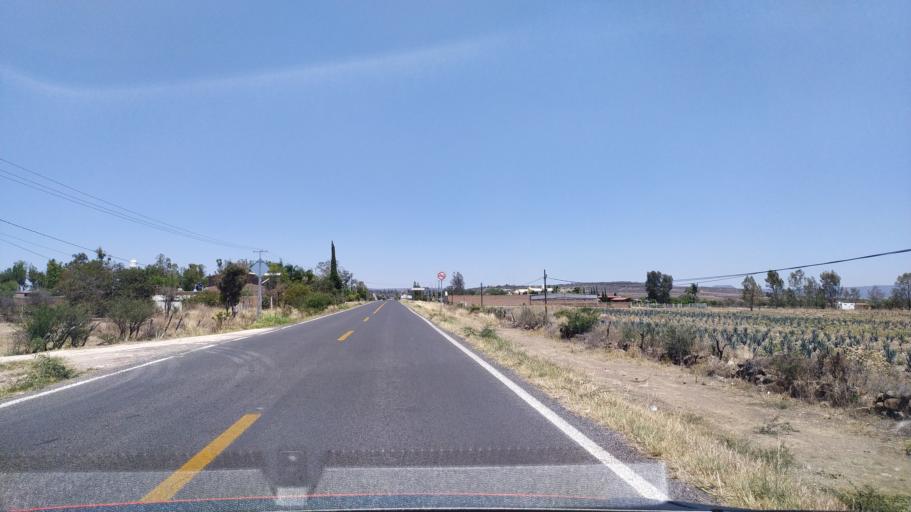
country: MX
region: Guanajuato
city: Ciudad Manuel Doblado
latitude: 20.8089
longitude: -101.9975
